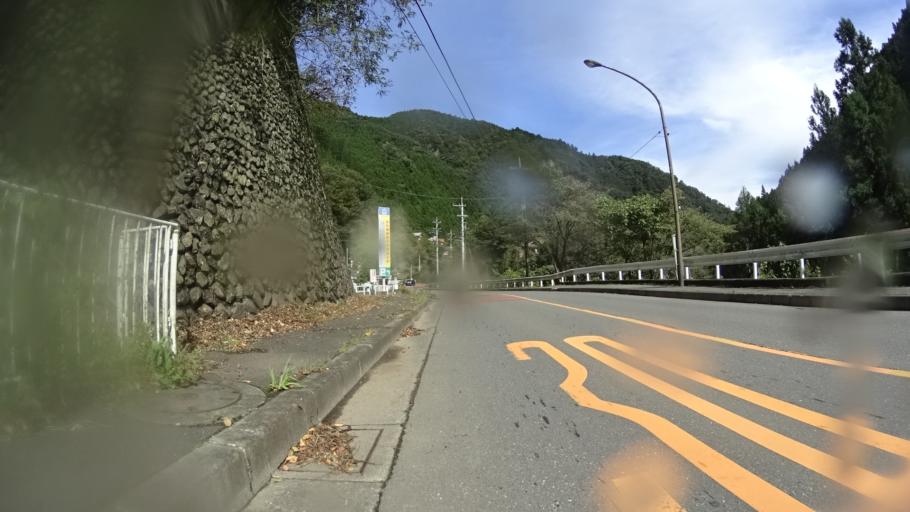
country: JP
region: Tokyo
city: Ome
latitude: 35.8092
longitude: 139.1137
